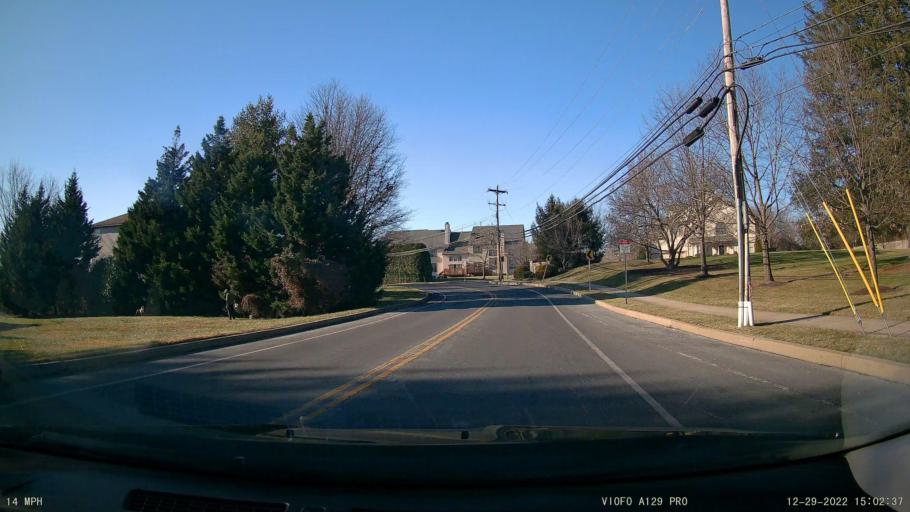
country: US
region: Pennsylvania
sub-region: Montgomery County
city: Norristown
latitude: 40.1341
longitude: -75.3080
